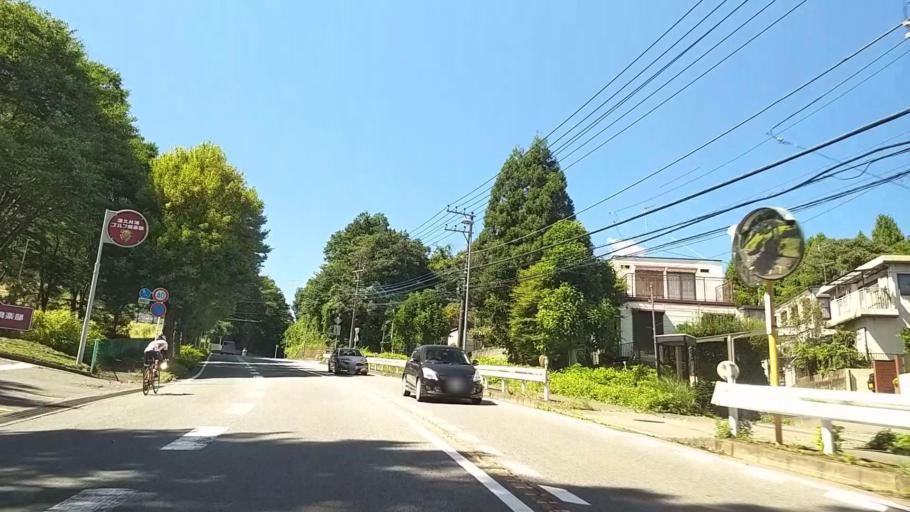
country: JP
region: Tokyo
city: Hachioji
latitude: 35.5878
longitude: 139.2392
